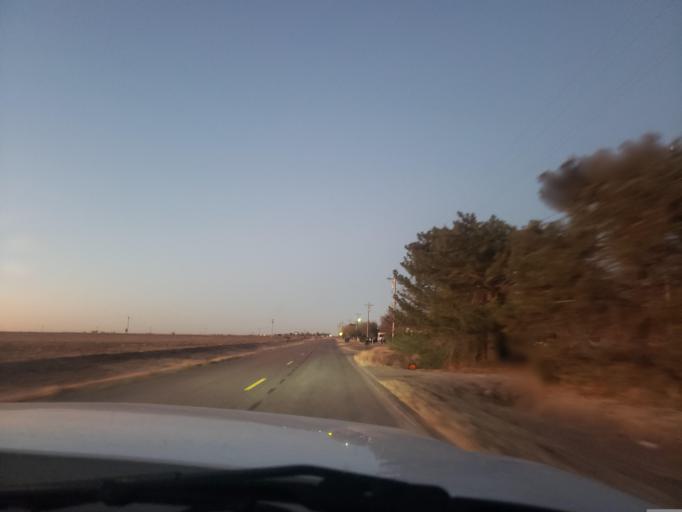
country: US
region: Kansas
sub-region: Finney County
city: Garden City
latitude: 37.9981
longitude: -100.8749
